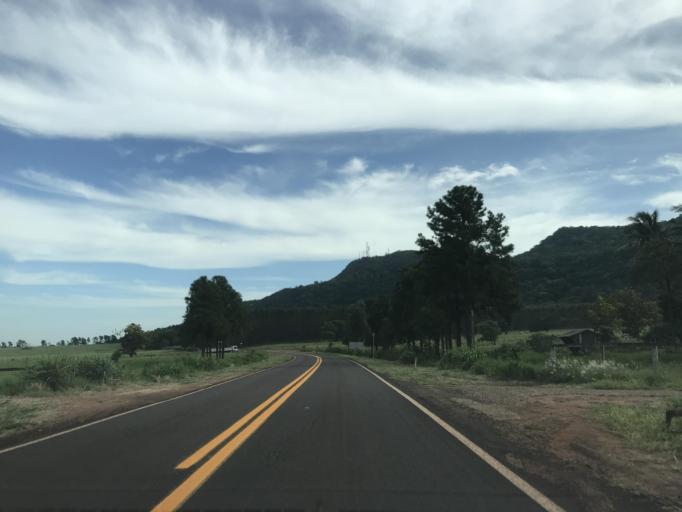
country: BR
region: Parana
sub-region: Terra Rica
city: Terra Rica
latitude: -22.7957
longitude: -52.6530
